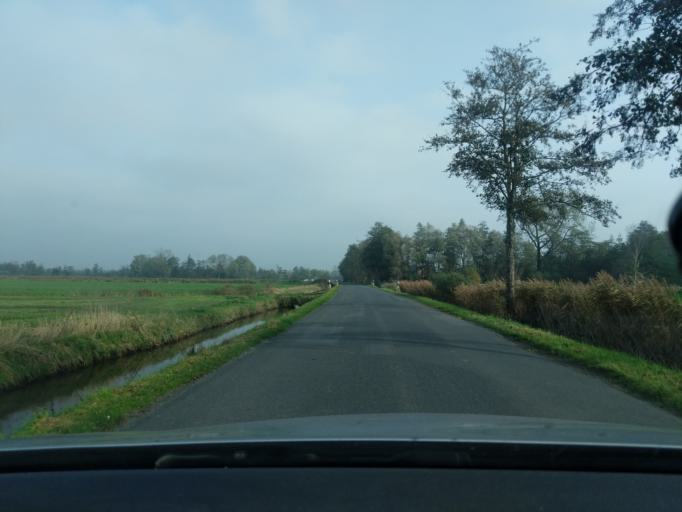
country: DE
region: Lower Saxony
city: Ihlienworth
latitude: 53.7345
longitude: 8.8941
